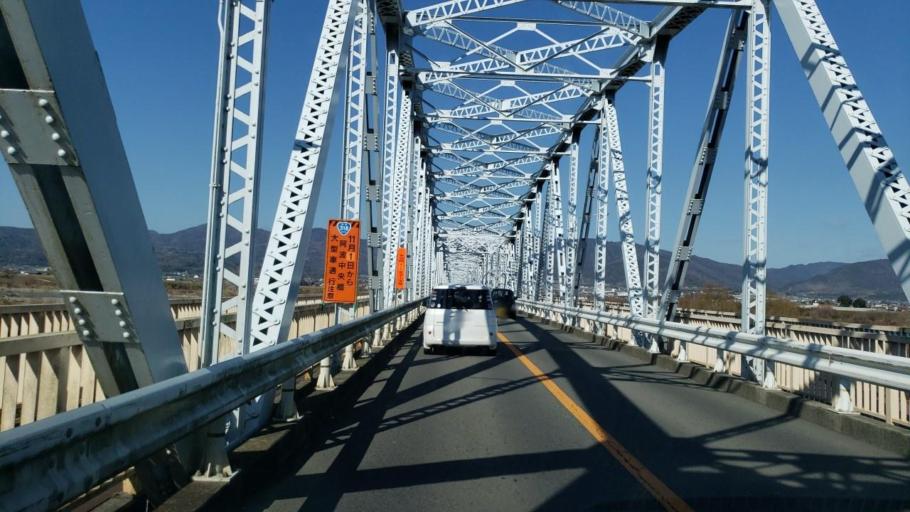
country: JP
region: Tokushima
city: Kamojimacho-jogejima
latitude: 34.0839
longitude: 134.3472
